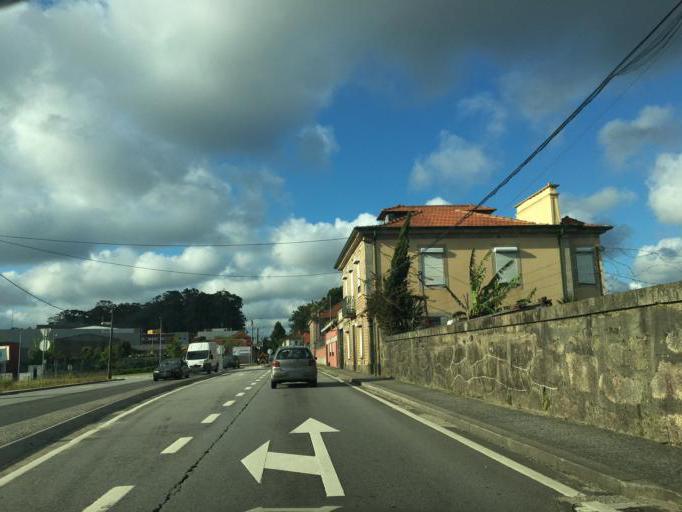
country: PT
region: Porto
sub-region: Maia
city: Anta
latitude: 41.2709
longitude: -8.6102
